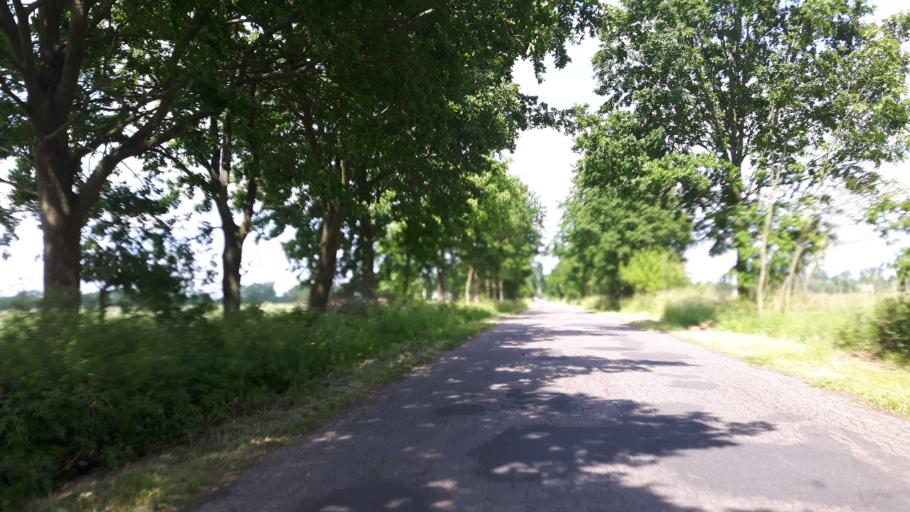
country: PL
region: West Pomeranian Voivodeship
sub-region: Powiat goleniowski
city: Osina
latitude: 53.6727
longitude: 14.9986
